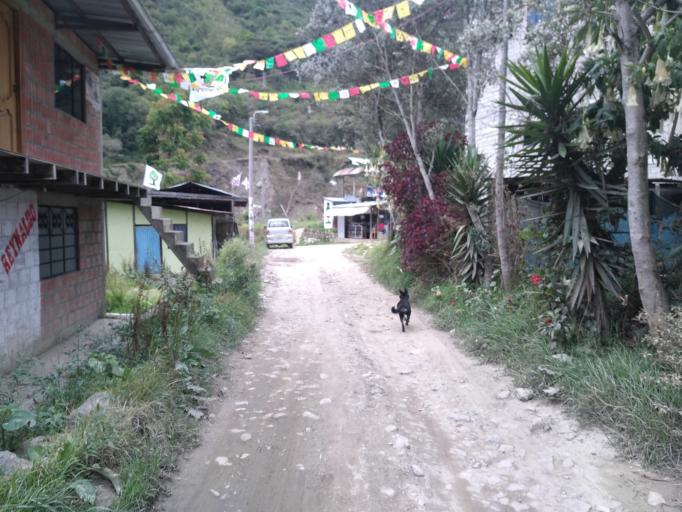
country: PE
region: Cusco
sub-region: Provincia de La Convencion
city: Santa Teresa
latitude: -13.2263
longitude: -72.6279
